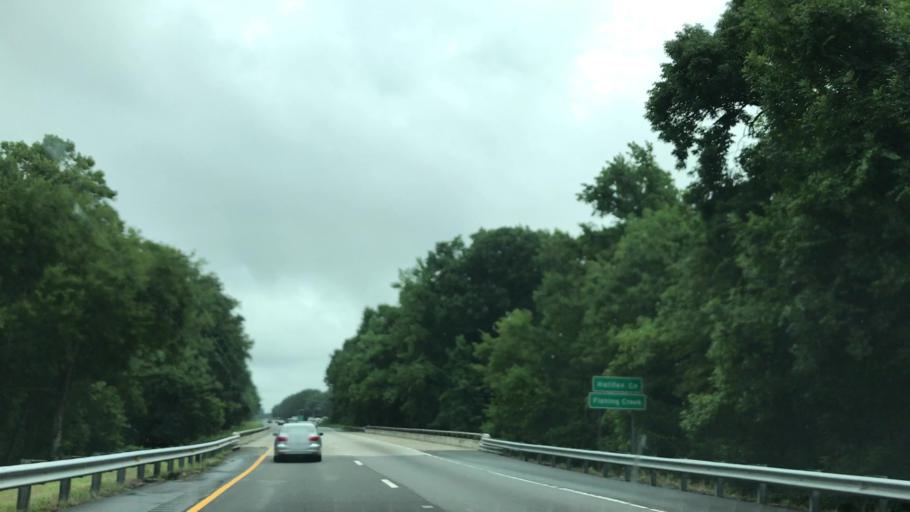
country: US
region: North Carolina
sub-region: Halifax County
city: Enfield
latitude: 36.1424
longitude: -77.7866
